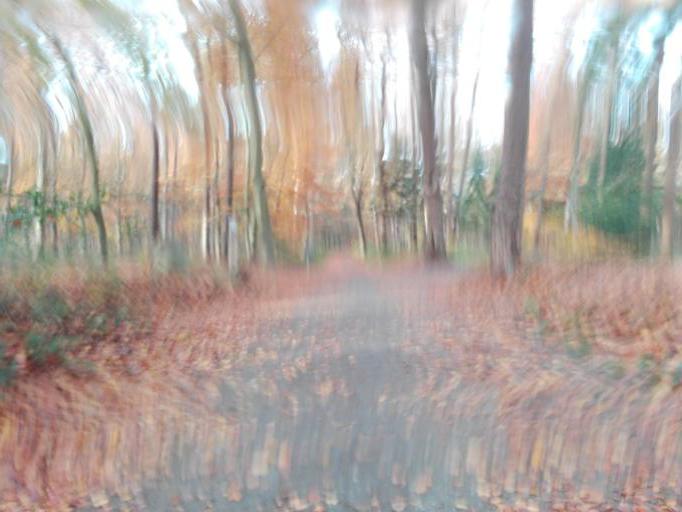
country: DE
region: Lower Saxony
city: Rastede
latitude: 53.2735
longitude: 8.1631
